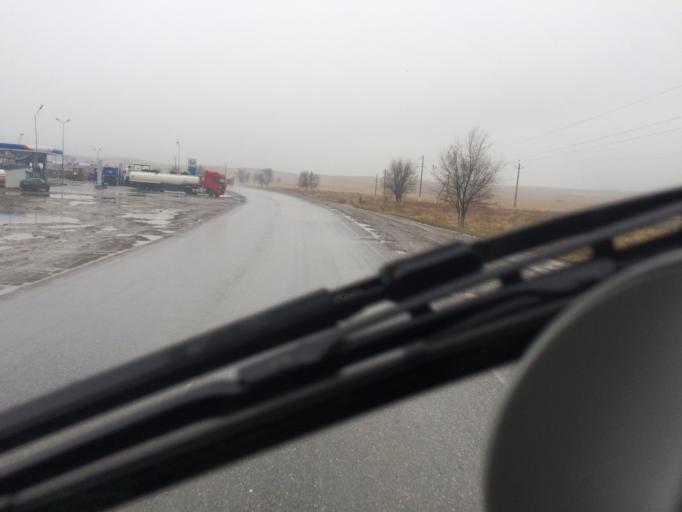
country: KG
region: Chuy
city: Kant
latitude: 43.0035
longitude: 74.8636
